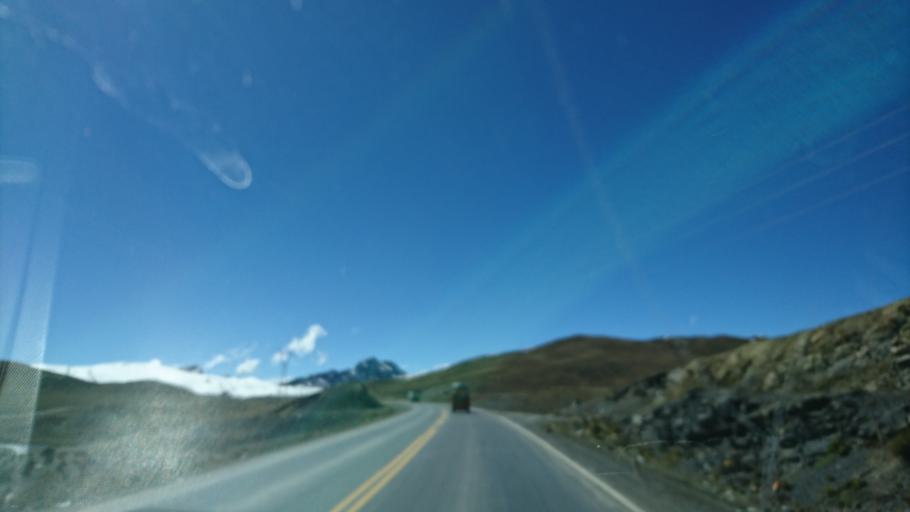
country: BO
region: La Paz
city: La Paz
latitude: -16.3660
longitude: -68.0446
